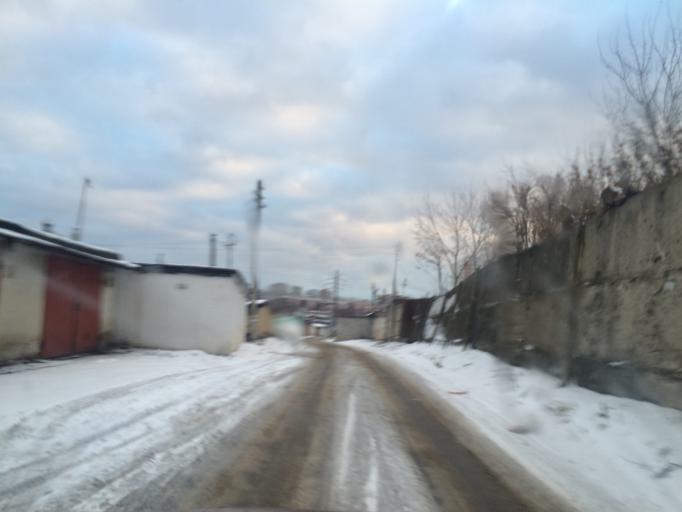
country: RU
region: Tula
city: Tula
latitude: 54.2187
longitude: 37.6823
